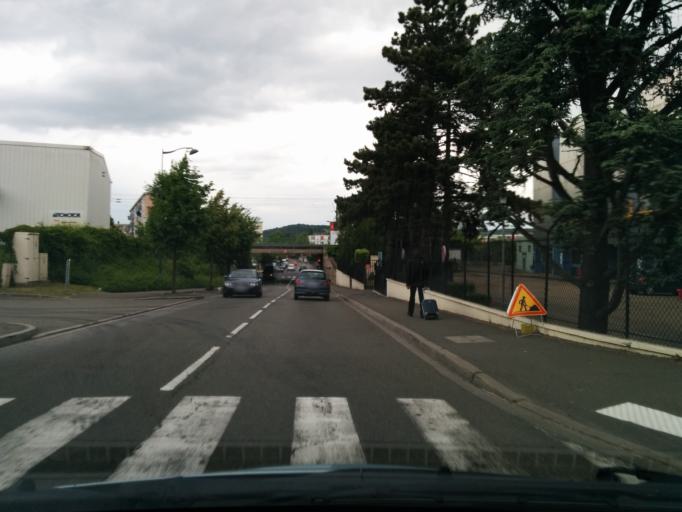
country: FR
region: Ile-de-France
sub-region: Departement des Yvelines
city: Buchelay
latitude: 48.9931
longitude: 1.6870
